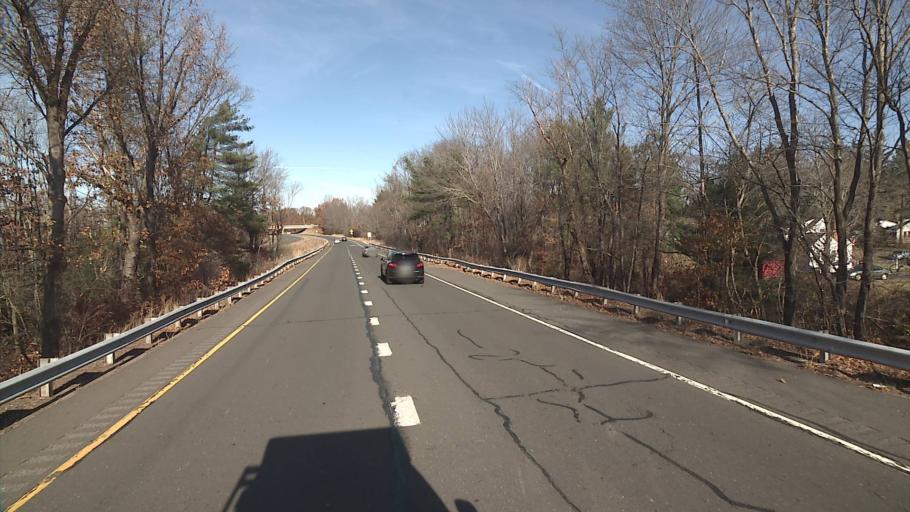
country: US
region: Connecticut
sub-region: Hartford County
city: Glastonbury Center
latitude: 41.7106
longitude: -72.5975
